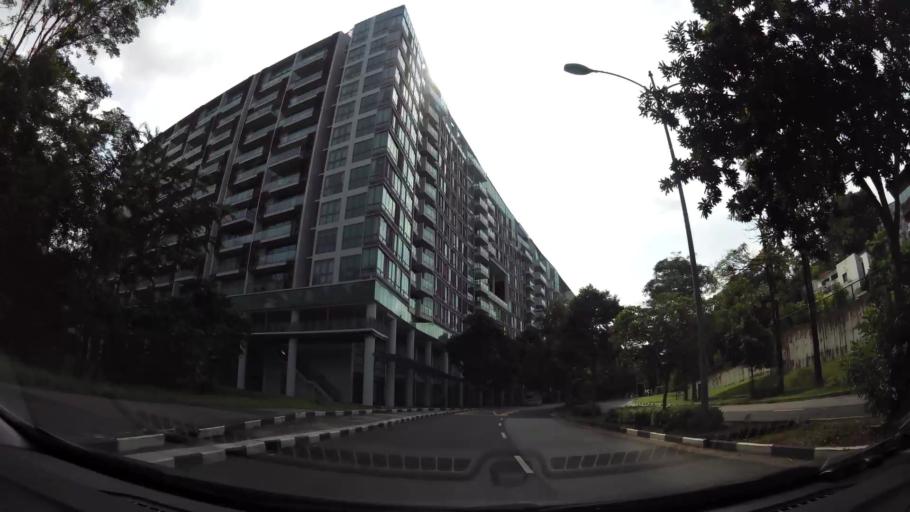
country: SG
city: Singapore
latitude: 1.3029
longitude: 103.7887
